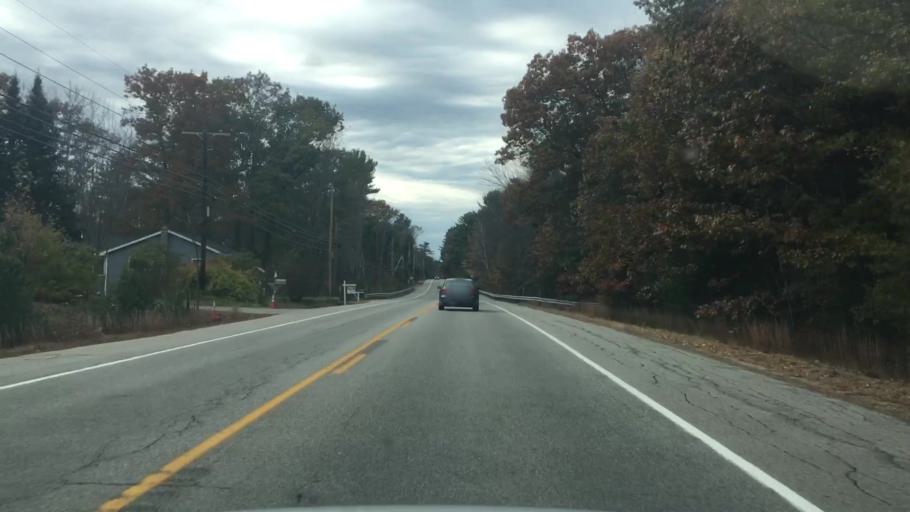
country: US
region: Maine
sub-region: York County
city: Alfred
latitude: 43.4764
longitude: -70.6759
